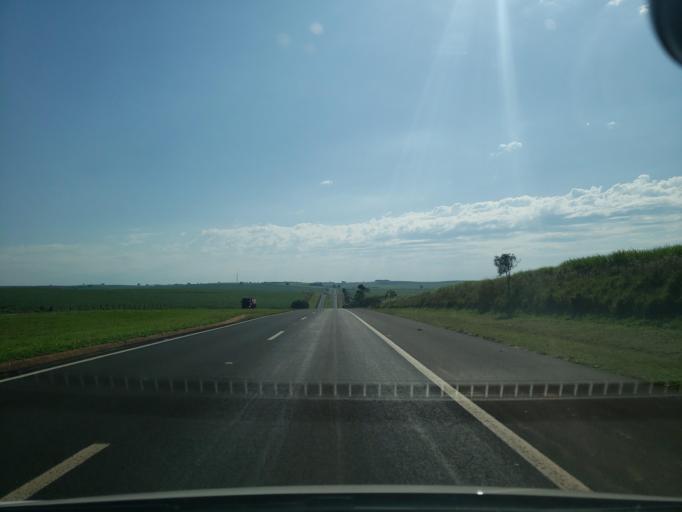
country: BR
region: Sao Paulo
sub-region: Promissao
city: Promissao
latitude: -21.5380
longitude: -49.9743
